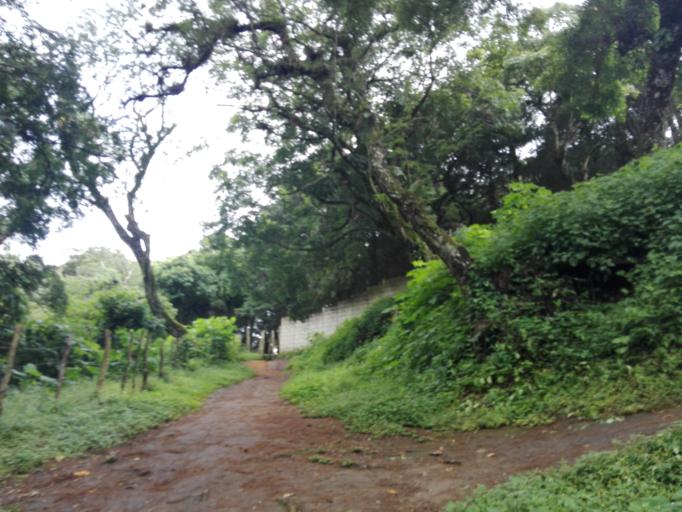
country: GT
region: Guatemala
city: Santa Catarina Pinula
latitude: 14.5292
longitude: -90.4946
